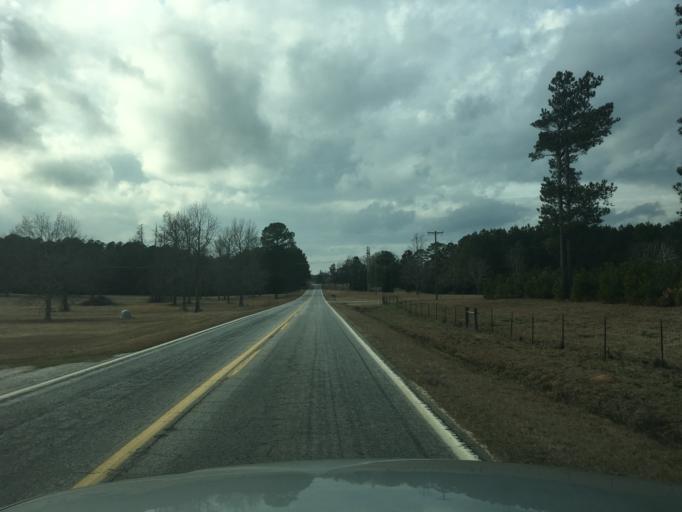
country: US
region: South Carolina
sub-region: Abbeville County
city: Abbeville
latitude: 34.2402
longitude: -82.4014
